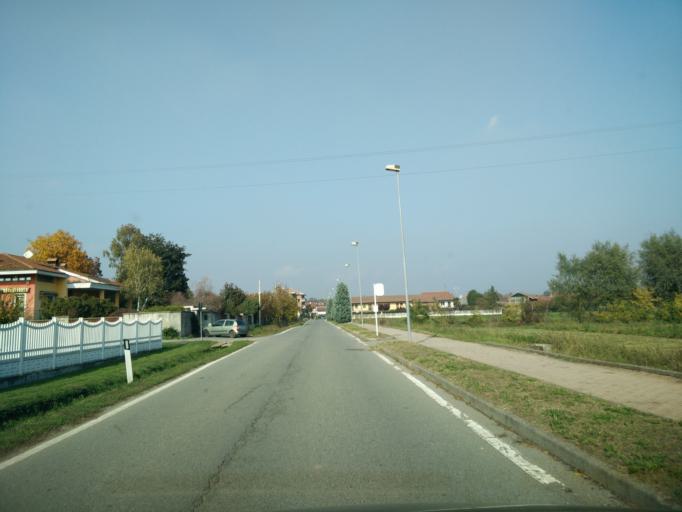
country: IT
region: Piedmont
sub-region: Provincia di Torino
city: Leini
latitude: 45.2010
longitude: 7.7167
